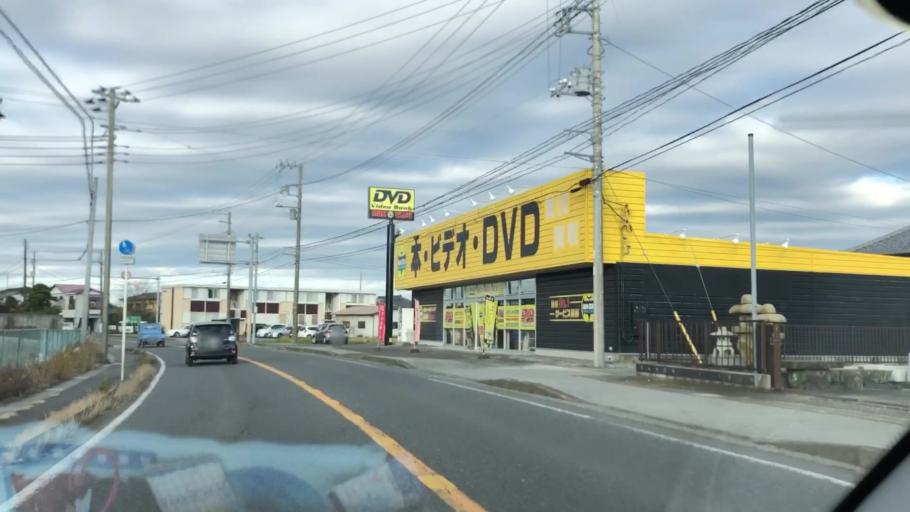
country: JP
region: Chiba
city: Tateyama
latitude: 34.9994
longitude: 139.9060
